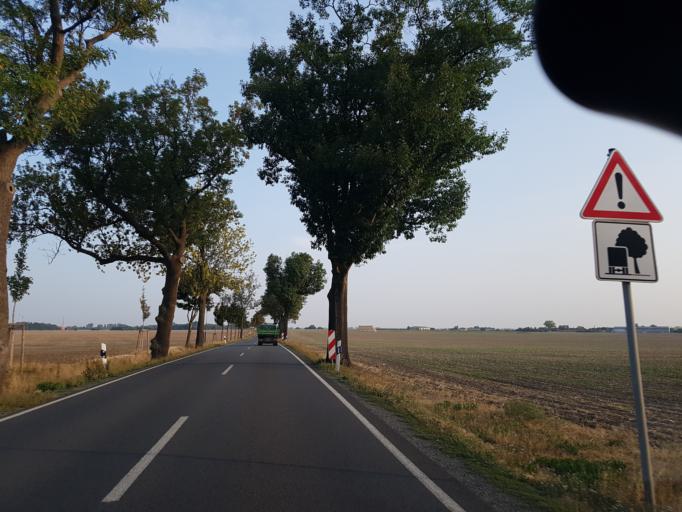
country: DE
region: Saxony
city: Elsnig
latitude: 51.6185
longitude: 12.9080
